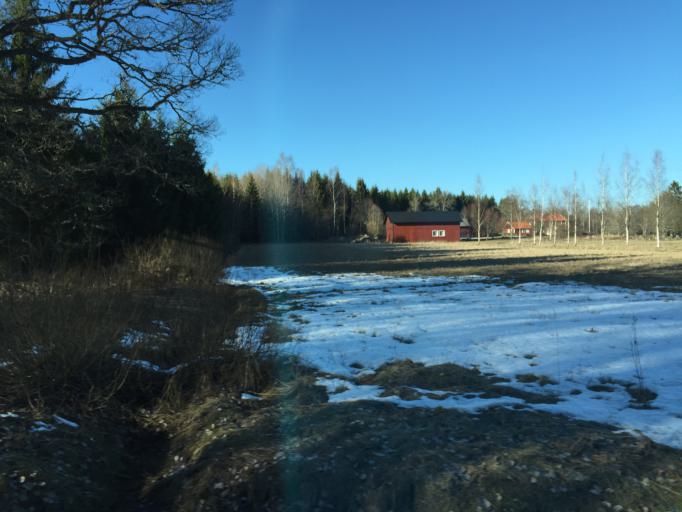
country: SE
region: Soedermanland
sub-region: Vingakers Kommun
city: Vingaker
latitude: 59.0362
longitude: 15.7089
